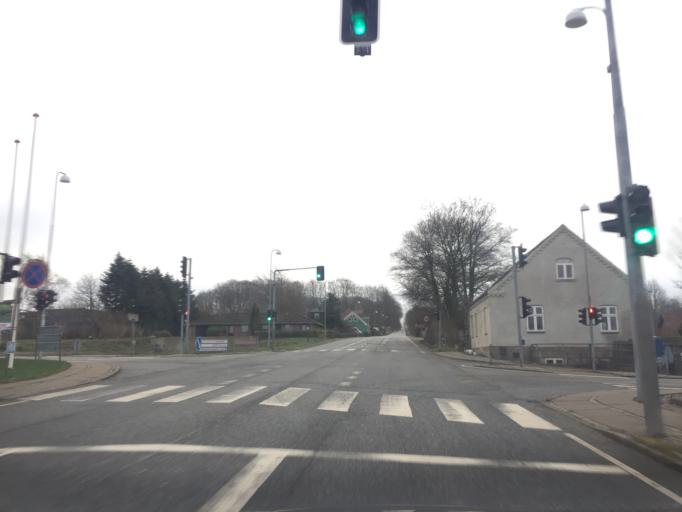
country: DK
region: South Denmark
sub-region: Svendborg Kommune
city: Thuro By
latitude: 55.1550
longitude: 10.6729
